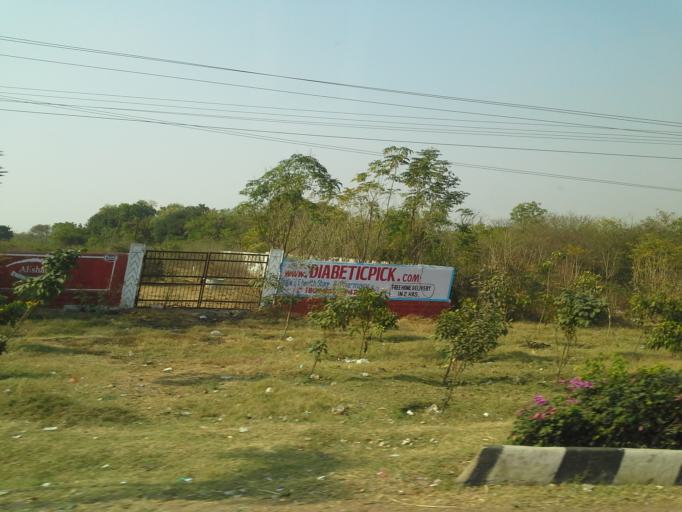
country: IN
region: Telangana
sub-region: Rangareddi
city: Balapur
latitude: 17.2739
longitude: 78.4000
